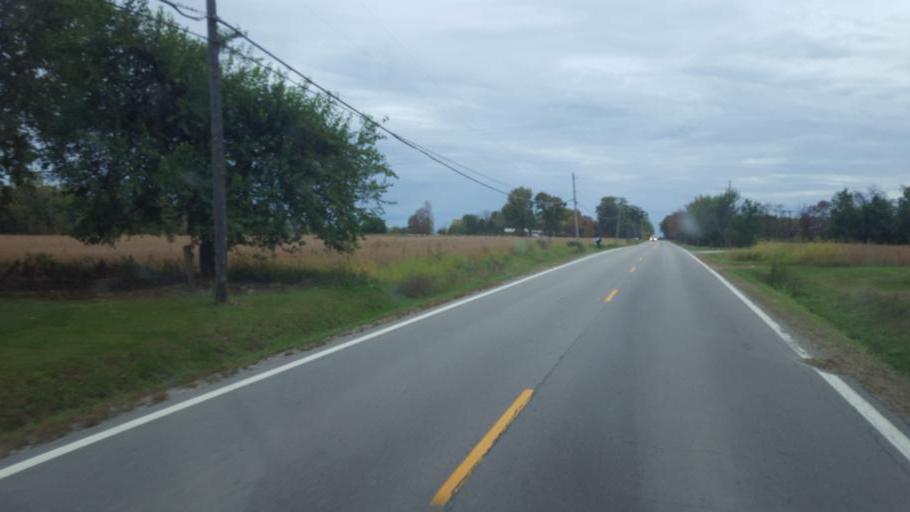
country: US
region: Ohio
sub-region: Huron County
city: Wakeman
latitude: 41.2902
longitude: -82.3773
